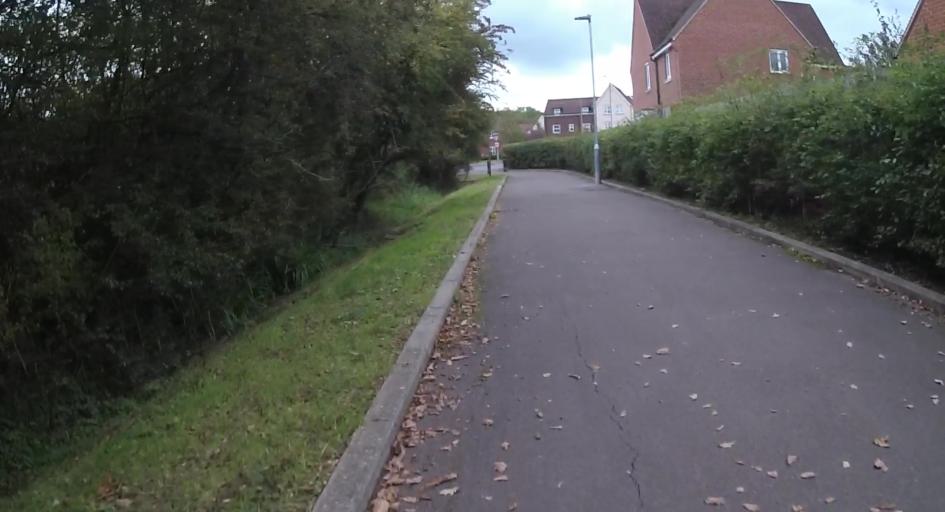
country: GB
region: England
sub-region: Bracknell Forest
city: Binfield
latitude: 51.4106
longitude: -0.7810
